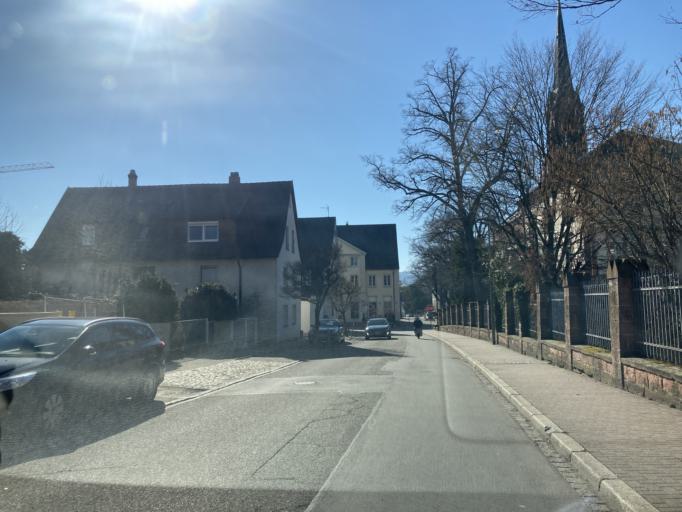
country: DE
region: Baden-Wuerttemberg
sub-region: Freiburg Region
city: Mullheim
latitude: 47.8094
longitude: 7.6266
